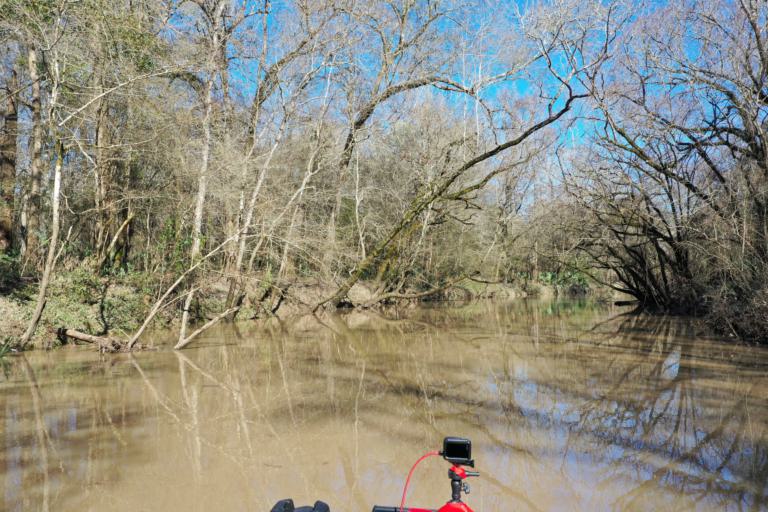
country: US
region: Louisiana
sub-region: Calcasieu Parish
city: Iowa
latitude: 30.3155
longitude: -93.0547
